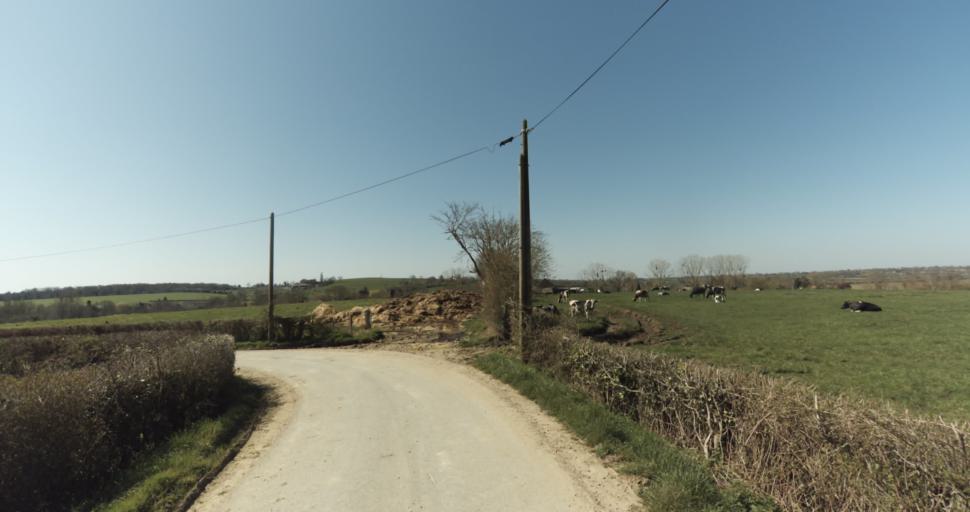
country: FR
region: Lower Normandy
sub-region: Departement du Calvados
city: Saint-Pierre-sur-Dives
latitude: 48.9904
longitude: 0.0353
